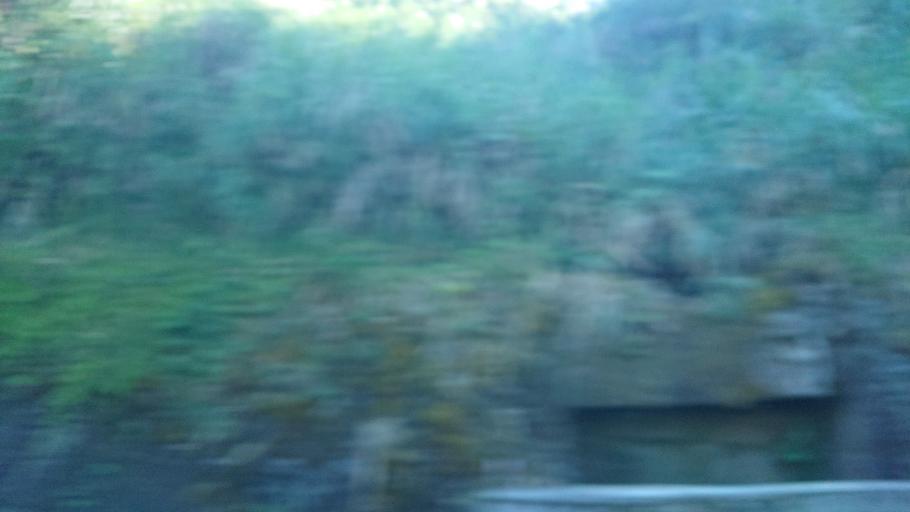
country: TW
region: Taiwan
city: Lugu
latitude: 23.4937
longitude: 120.7929
